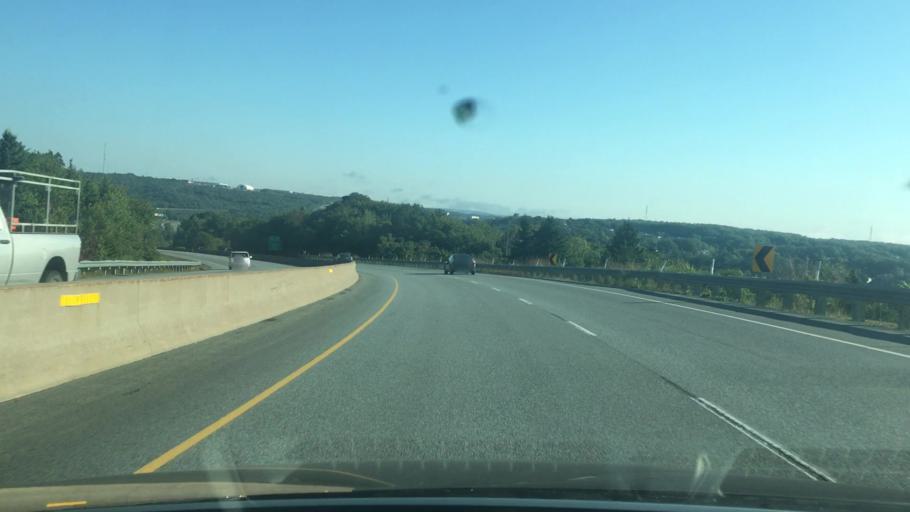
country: CA
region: Nova Scotia
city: Dartmouth
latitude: 44.7354
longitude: -63.6627
